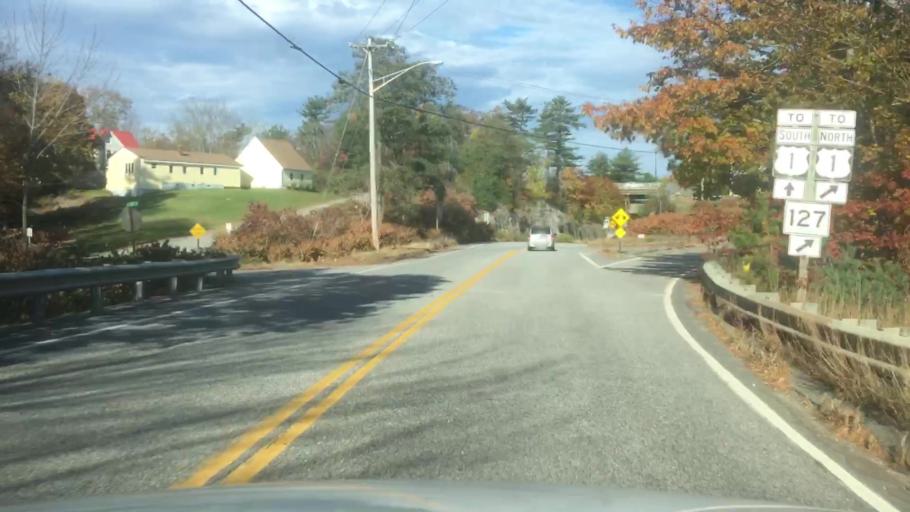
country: US
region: Maine
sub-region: Sagadahoc County
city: Woolwich
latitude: 43.9101
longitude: -69.8014
